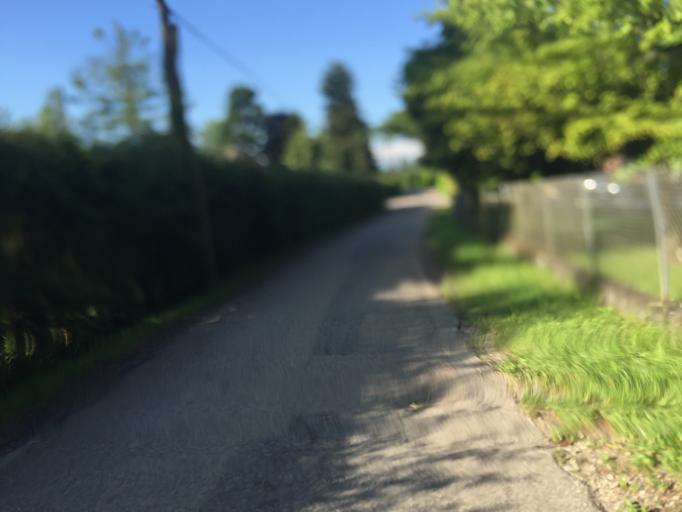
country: FR
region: Rhone-Alpes
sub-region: Departement de la Savoie
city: Drumettaz-Clarafond
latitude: 45.6662
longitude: 5.9328
